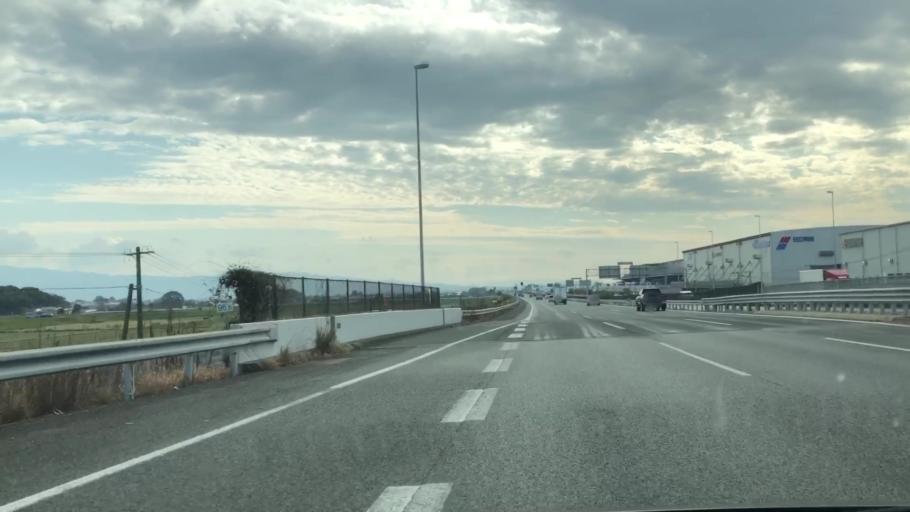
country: JP
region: Saga Prefecture
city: Tosu
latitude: 33.3922
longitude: 130.5384
